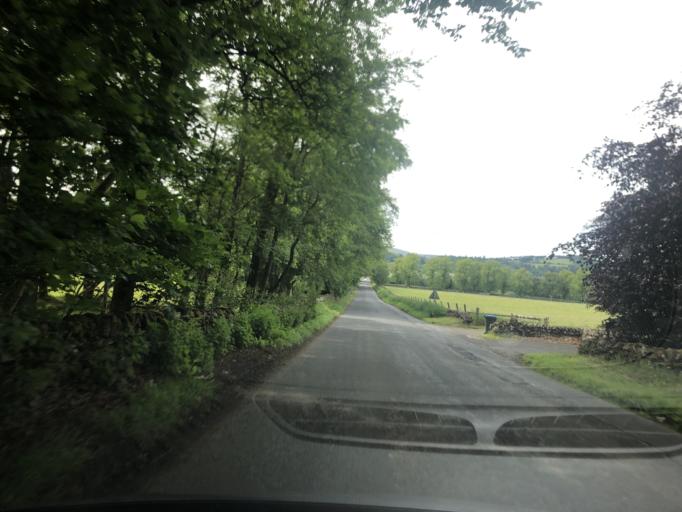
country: GB
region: Scotland
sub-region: The Scottish Borders
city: West Linton
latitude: 55.7421
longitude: -3.3418
